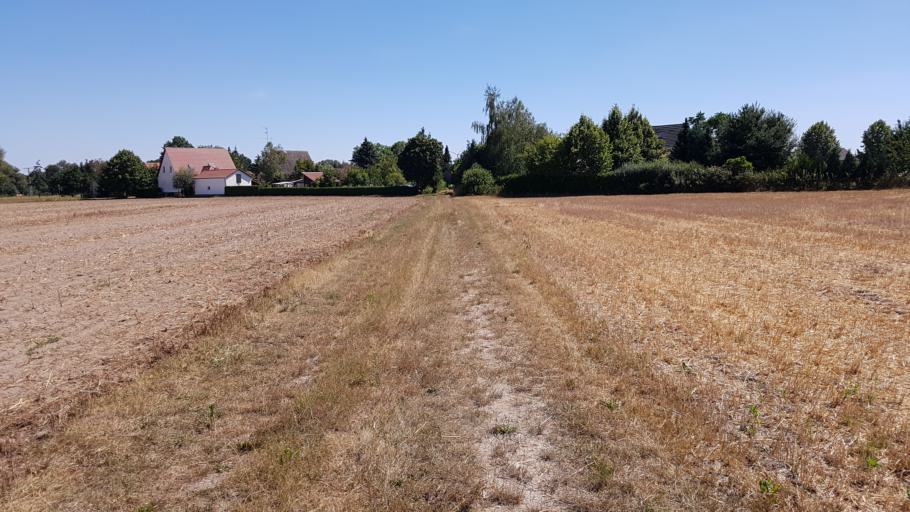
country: DE
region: Brandenburg
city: Finsterwalde
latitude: 51.6649
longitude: 13.7113
